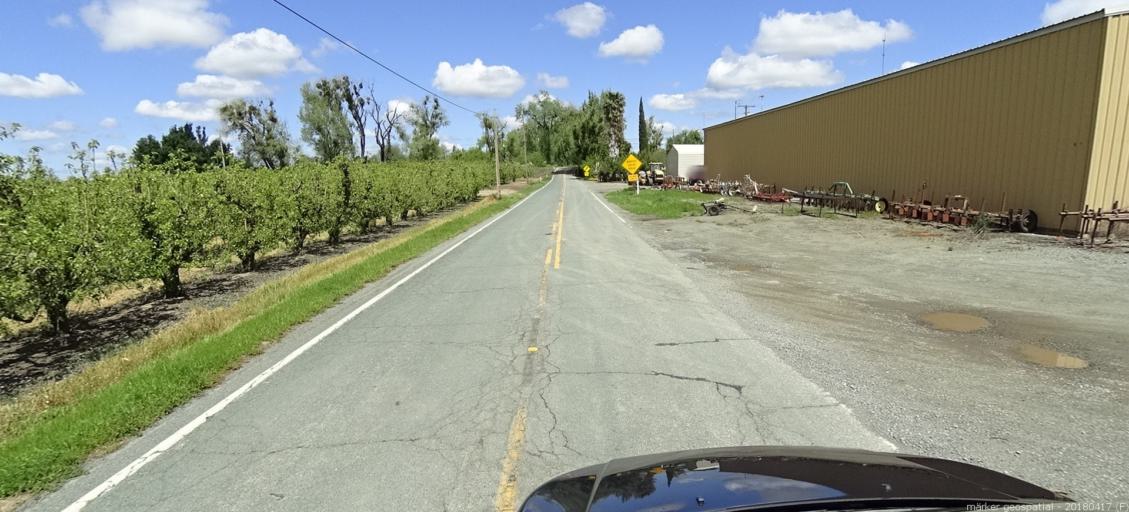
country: US
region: California
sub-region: Sacramento County
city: Walnut Grove
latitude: 38.2239
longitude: -121.5273
